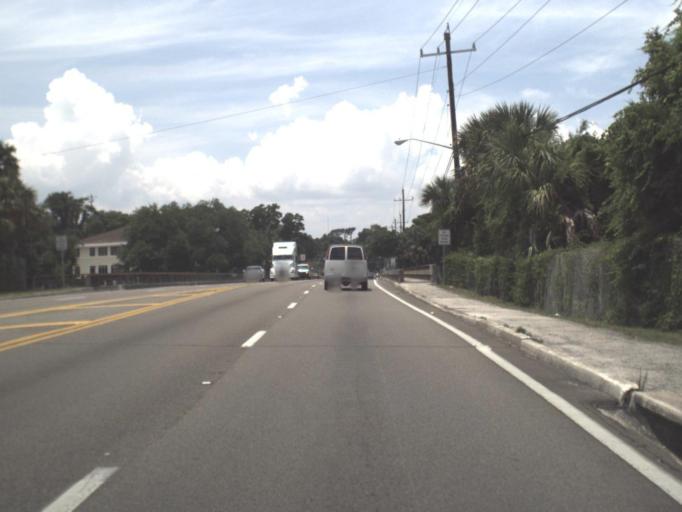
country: US
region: Florida
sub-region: Duval County
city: Jacksonville
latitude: 30.3128
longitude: -81.5944
